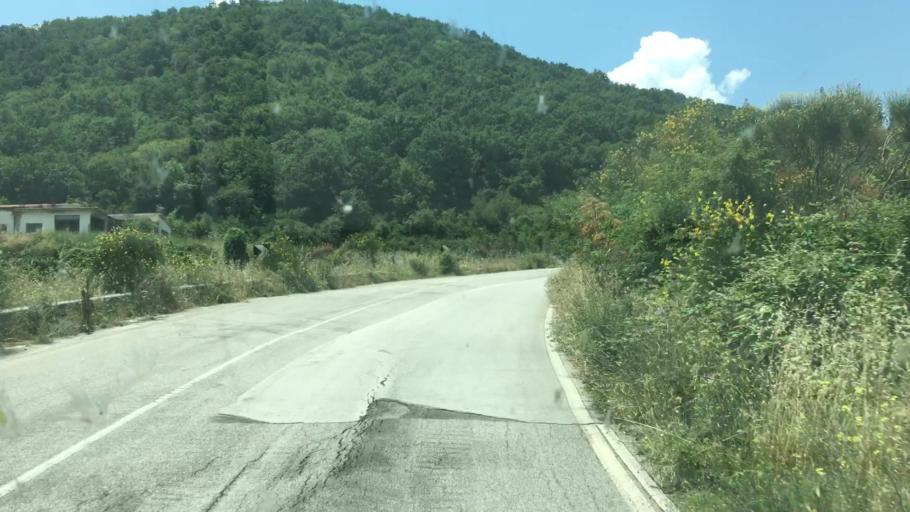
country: IT
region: Basilicate
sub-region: Provincia di Potenza
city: Tolve
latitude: 40.6865
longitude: 15.9833
